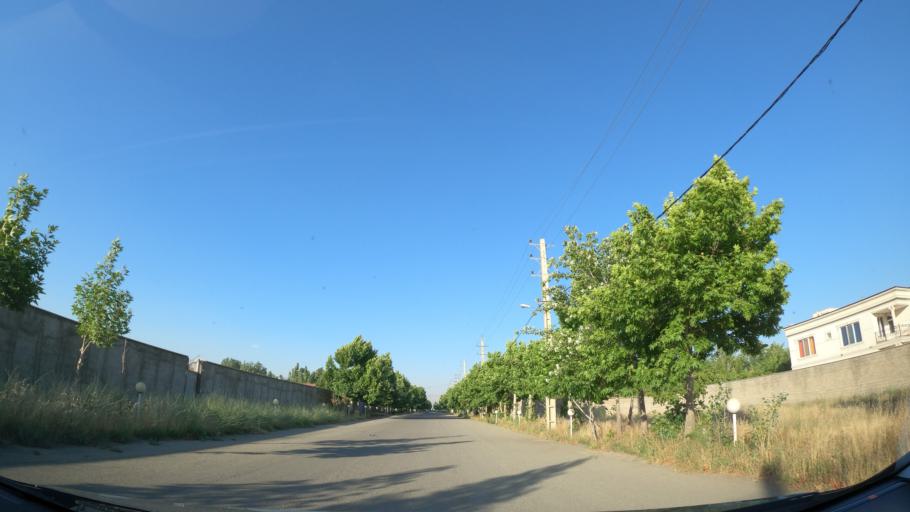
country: IR
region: Alborz
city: Hashtgerd
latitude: 35.9120
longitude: 50.7242
